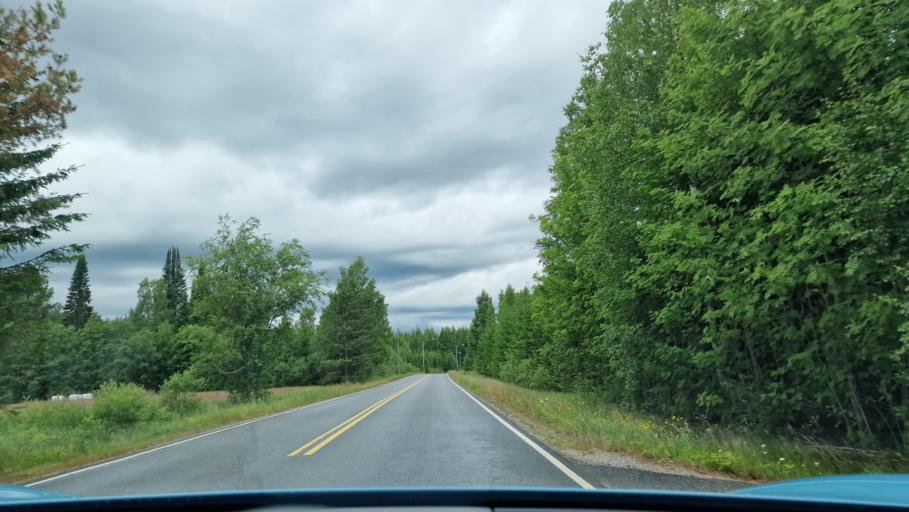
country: FI
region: Southern Ostrobothnia
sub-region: Jaerviseutu
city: Soini
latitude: 62.6965
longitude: 24.4556
